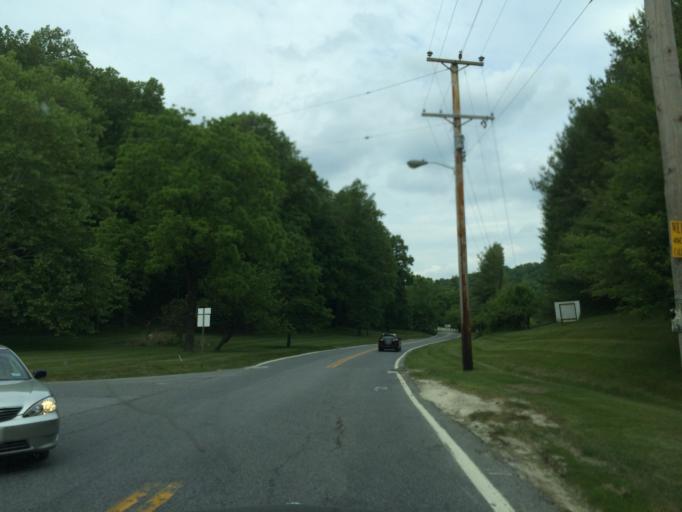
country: US
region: Maryland
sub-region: Baltimore County
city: Randallstown
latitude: 39.3675
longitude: -76.8762
